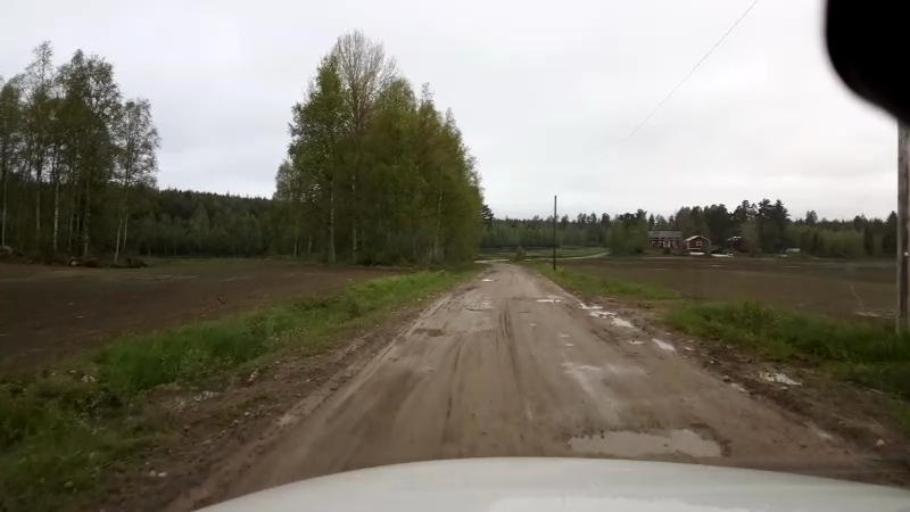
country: SE
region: Gaevleborg
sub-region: Ljusdals Kommun
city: Jaervsoe
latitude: 61.7716
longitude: 16.1990
